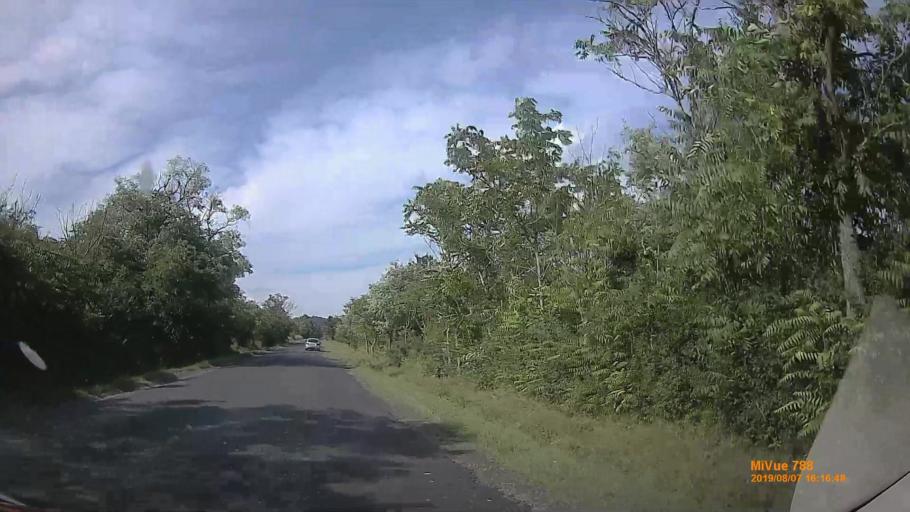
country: HU
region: Zala
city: Gyenesdias
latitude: 46.8178
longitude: 17.2705
